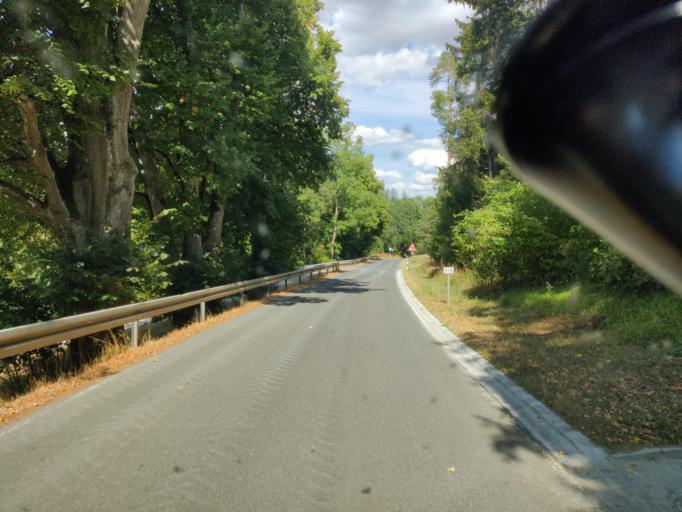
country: DE
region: Bavaria
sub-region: Regierungsbezirk Mittelfranken
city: Thalmassing
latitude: 49.0683
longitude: 11.2506
